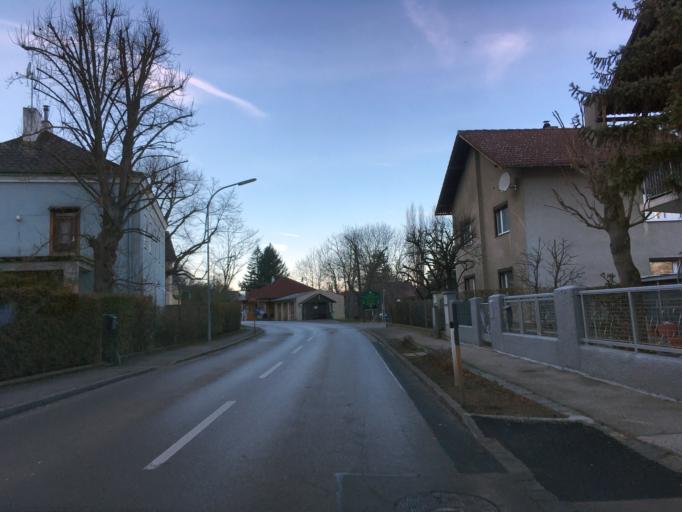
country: AT
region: Lower Austria
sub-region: Politischer Bezirk Korneuburg
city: Spillern
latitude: 48.3497
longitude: 16.2705
